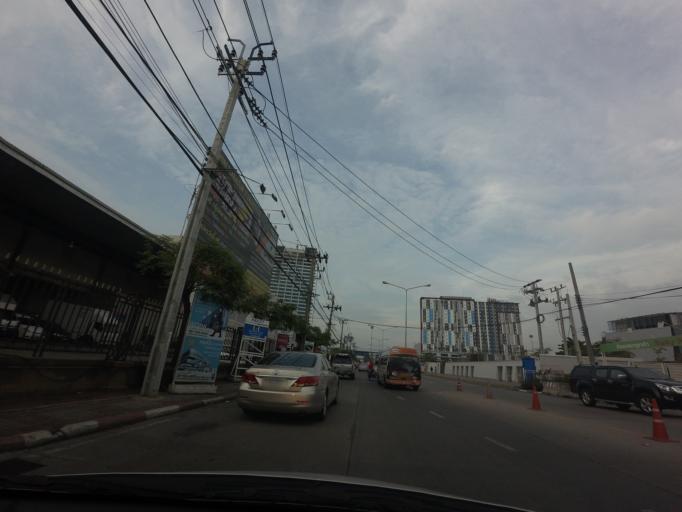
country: TH
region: Bangkok
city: Lak Si
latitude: 13.9141
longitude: 100.5505
